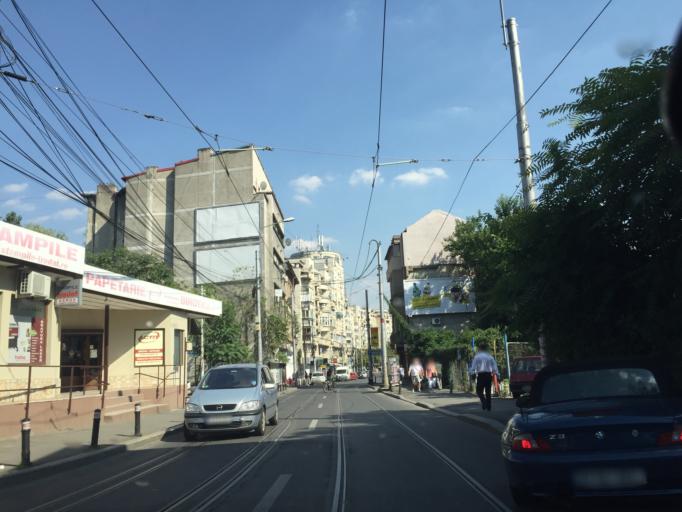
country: RO
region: Bucuresti
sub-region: Municipiul Bucuresti
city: Bucharest
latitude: 44.4312
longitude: 26.1055
